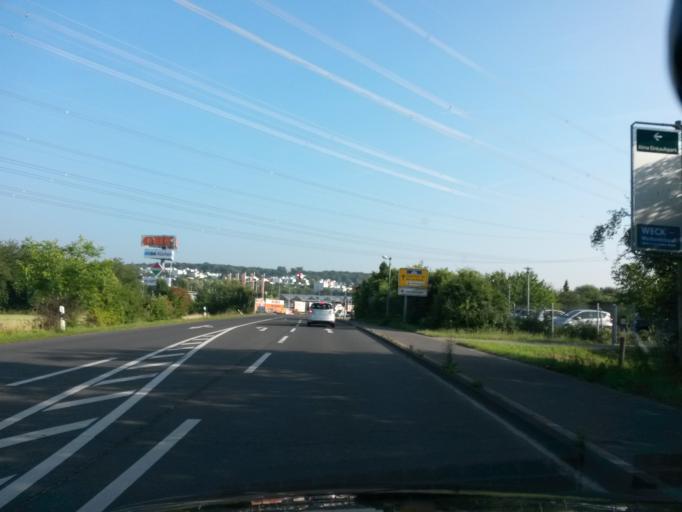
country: DE
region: North Rhine-Westphalia
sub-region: Regierungsbezirk Koln
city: Alfter
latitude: 50.7194
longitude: 7.0297
